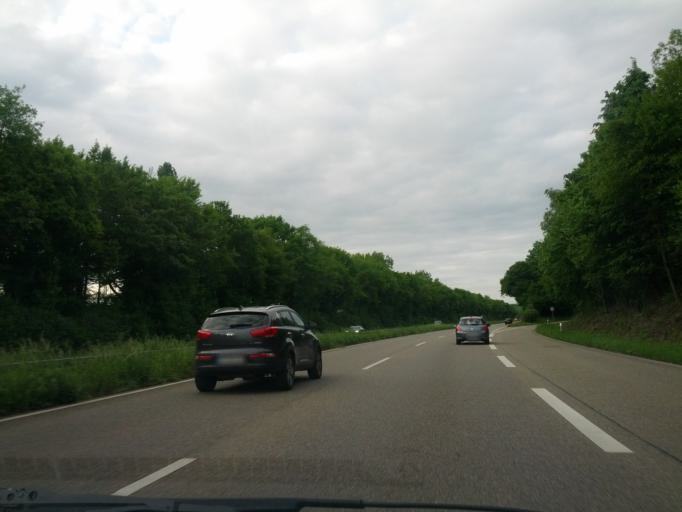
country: DE
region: Baden-Wuerttemberg
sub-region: Freiburg Region
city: Gundelfingen
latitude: 48.0252
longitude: 7.8567
